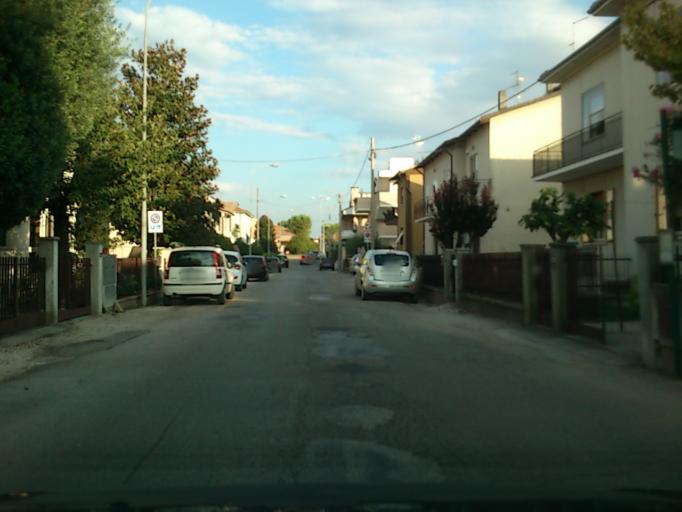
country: IT
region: The Marches
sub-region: Provincia di Pesaro e Urbino
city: Centinarola
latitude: 43.8327
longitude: 12.9992
